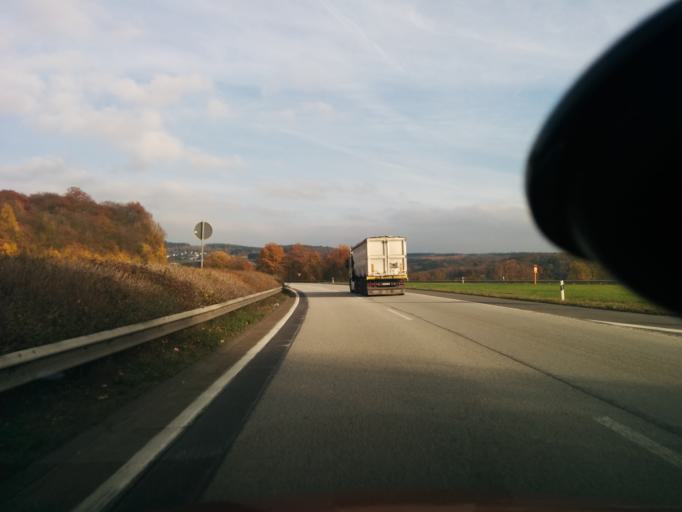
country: DE
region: Rheinland-Pfalz
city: Hohr-Grenzhausen
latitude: 50.4438
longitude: 7.6650
